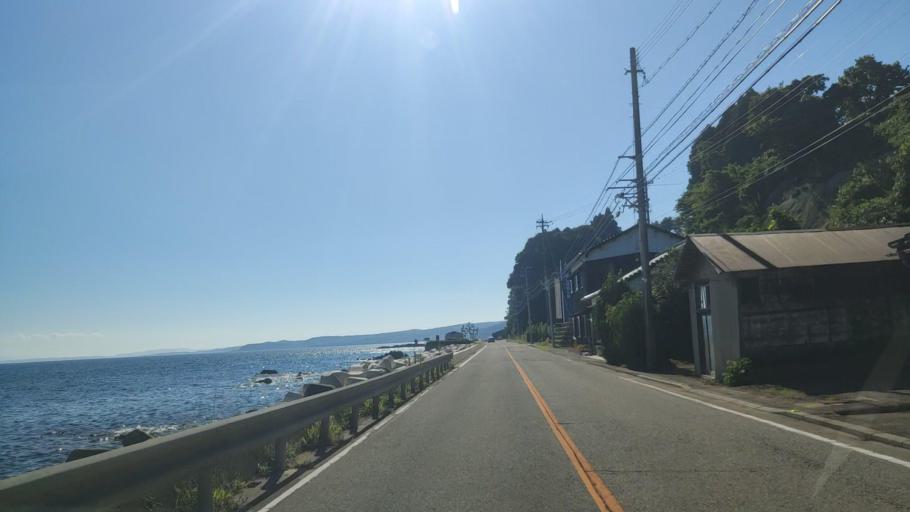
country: JP
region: Ishikawa
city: Nanao
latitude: 37.2938
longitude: 137.1352
